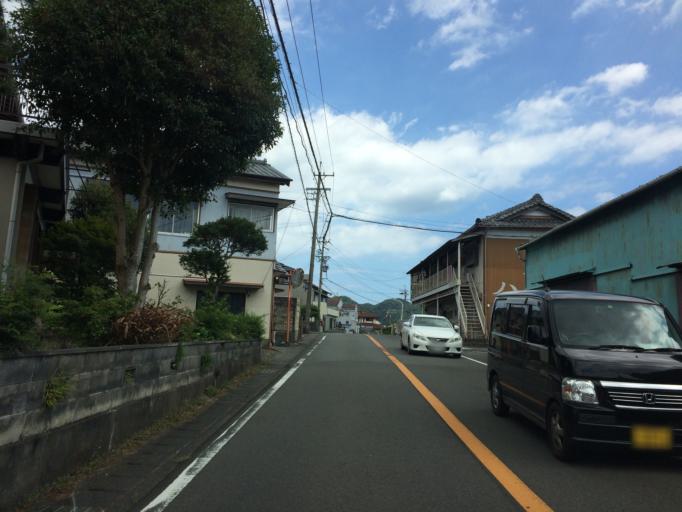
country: JP
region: Shizuoka
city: Yaizu
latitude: 34.8921
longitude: 138.3078
